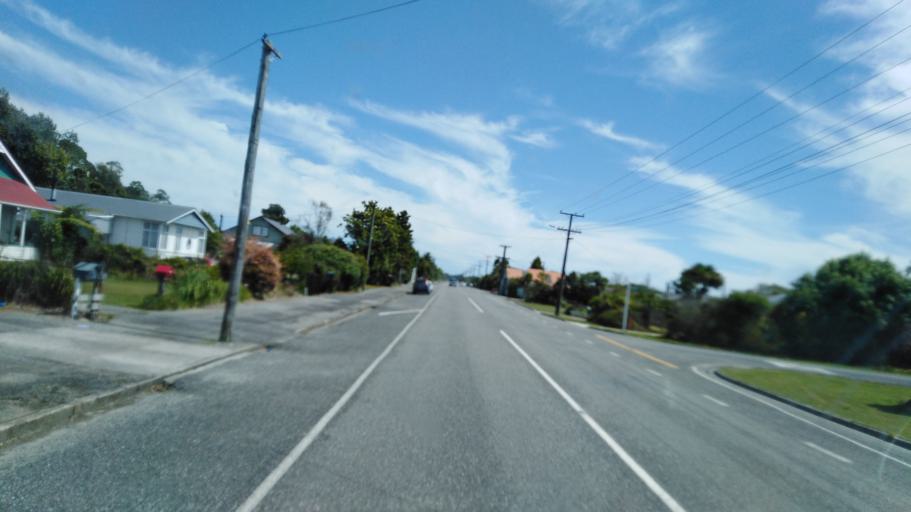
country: NZ
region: West Coast
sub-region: Buller District
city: Westport
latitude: -41.7525
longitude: 171.6221
